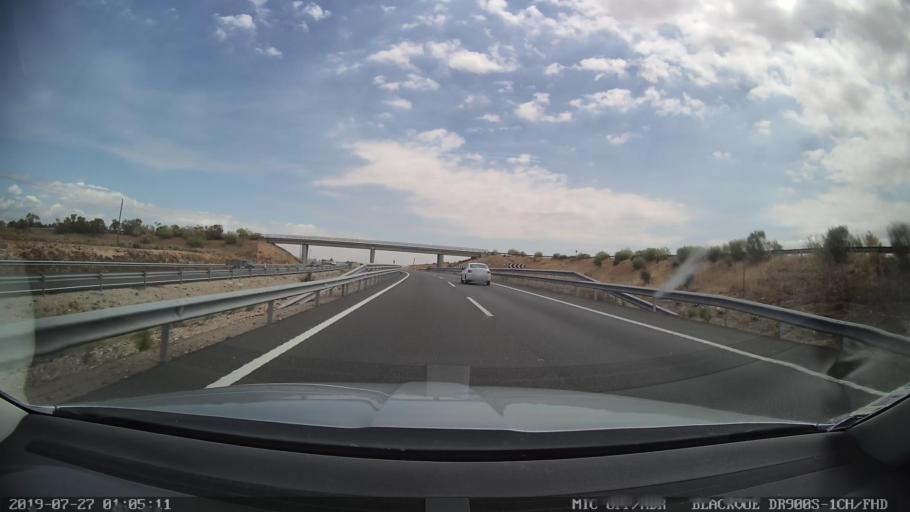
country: ES
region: Castille-La Mancha
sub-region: Province of Toledo
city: Cazalegas
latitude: 39.9985
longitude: -4.6450
